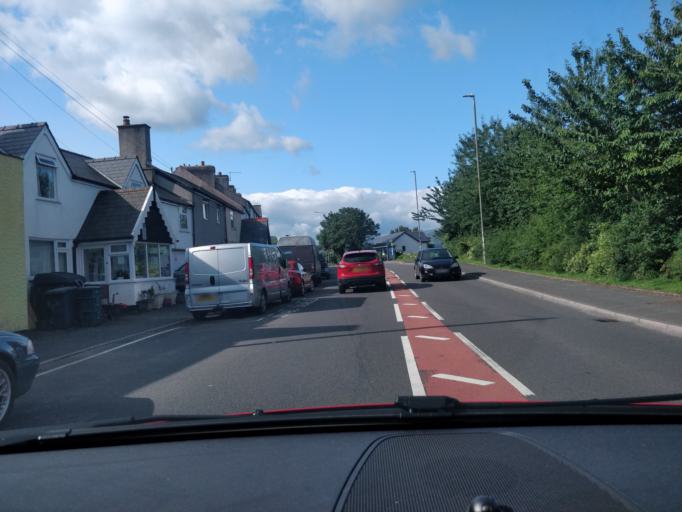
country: GB
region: Wales
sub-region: Conwy
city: Llansantffraid Glan Conwy
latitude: 53.2695
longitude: -3.7958
